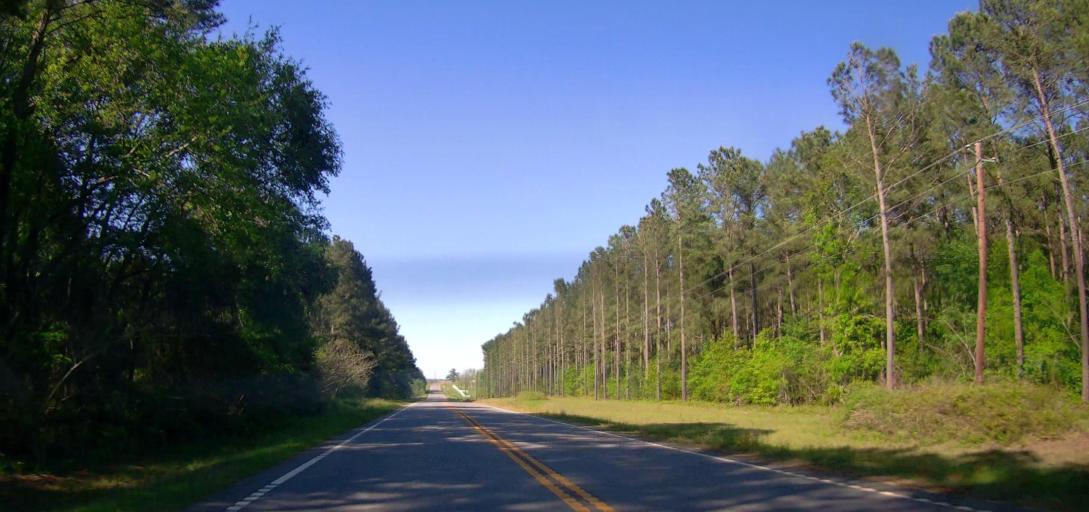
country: US
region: Georgia
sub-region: Pulaski County
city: Hawkinsville
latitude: 32.1678
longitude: -83.5117
